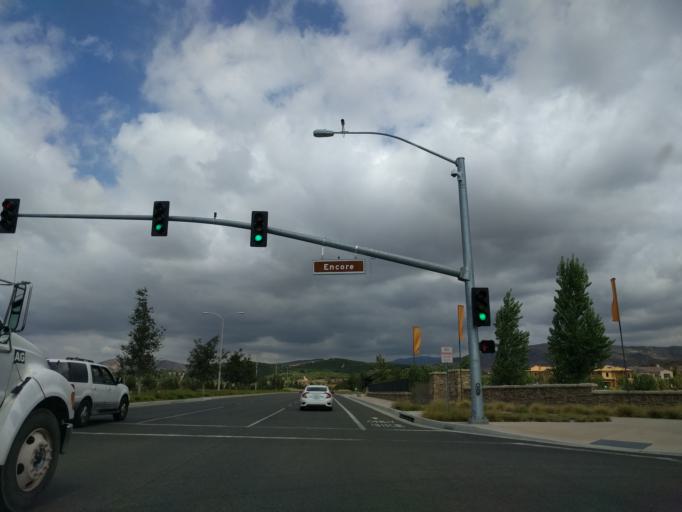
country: US
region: California
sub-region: Orange County
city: North Tustin
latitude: 33.7129
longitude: -117.7452
